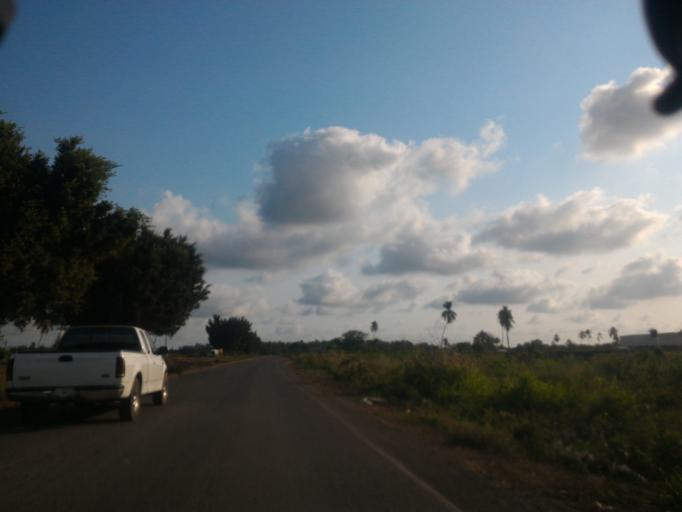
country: MX
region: Colima
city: Tecoman
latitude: 18.9154
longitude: -103.8541
